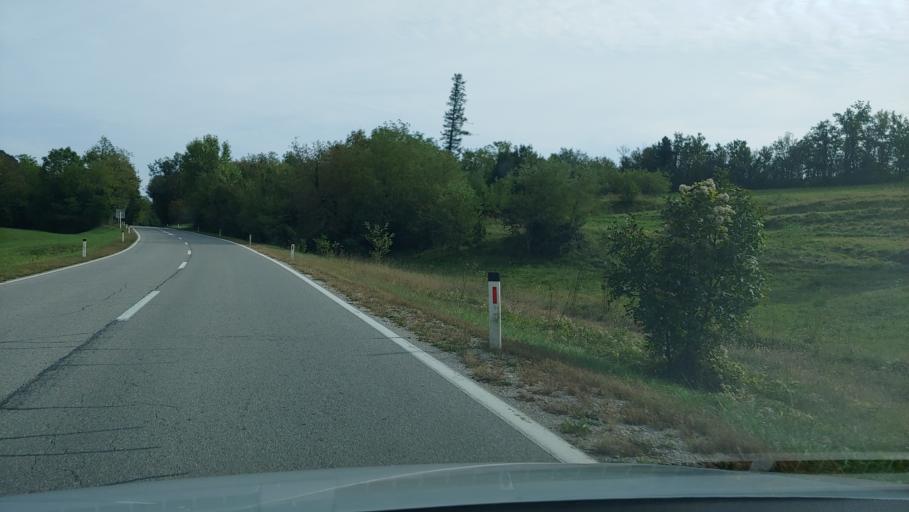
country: SI
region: Nova Gorica
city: Sempas
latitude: 45.9165
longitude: 13.7636
